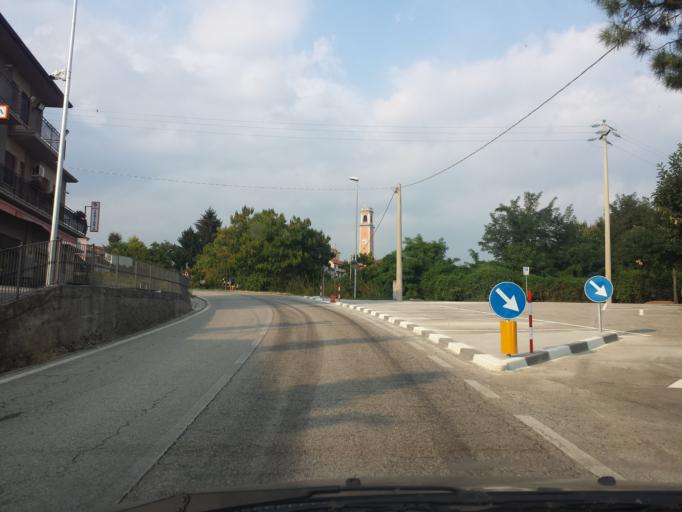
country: IT
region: Veneto
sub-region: Provincia di Vicenza
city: Mason Vicentino
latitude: 45.7280
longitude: 11.5825
